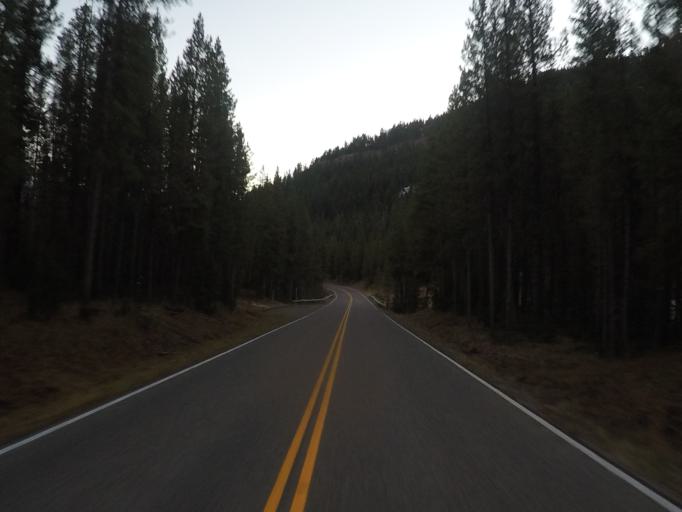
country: US
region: Montana
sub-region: Stillwater County
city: Absarokee
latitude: 44.9458
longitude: -110.0816
